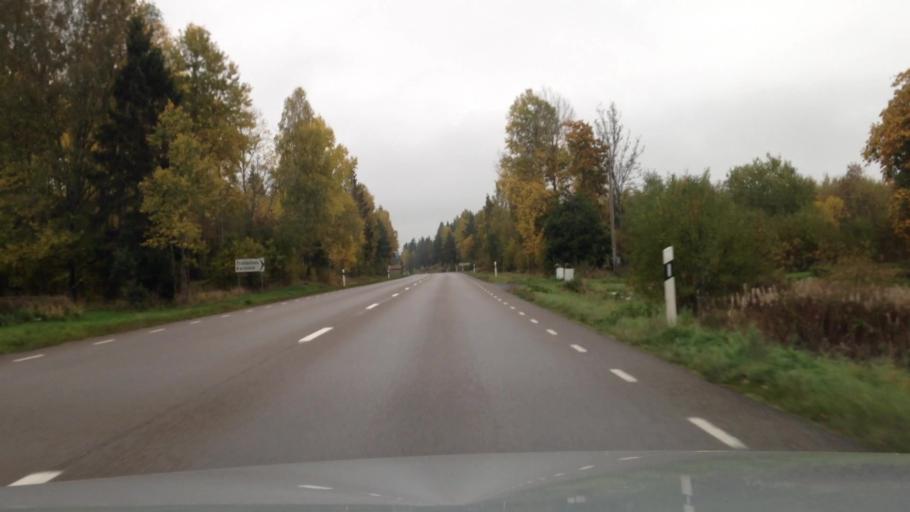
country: SE
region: Vaestra Goetaland
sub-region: Falkopings Kommun
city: Falkoeping
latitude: 58.2639
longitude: 13.4967
